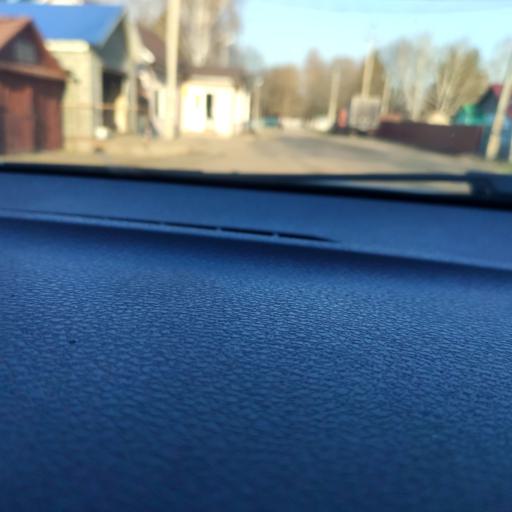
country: RU
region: Bashkortostan
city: Ulukulevo
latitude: 54.3768
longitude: 56.4501
